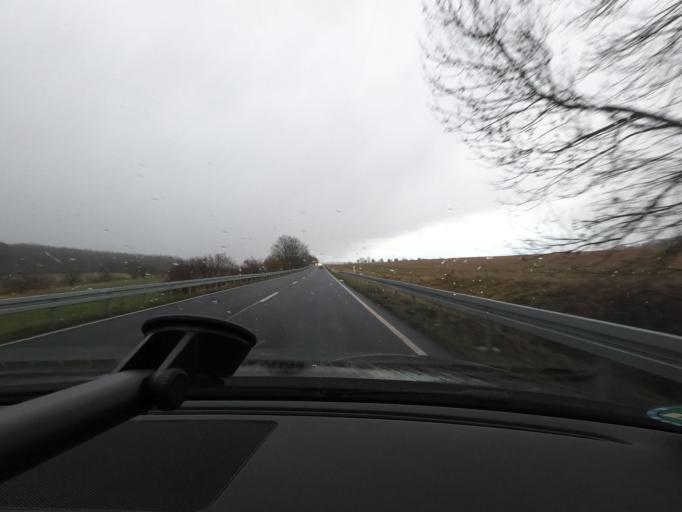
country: DE
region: Thuringia
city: Helmsdorf
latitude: 51.2718
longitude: 10.3744
